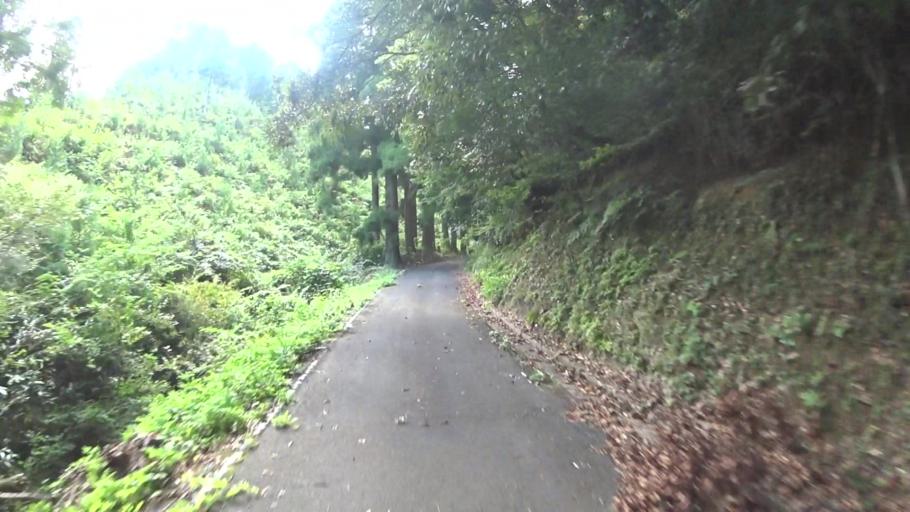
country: JP
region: Kyoto
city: Miyazu
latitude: 35.6671
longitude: 135.1366
